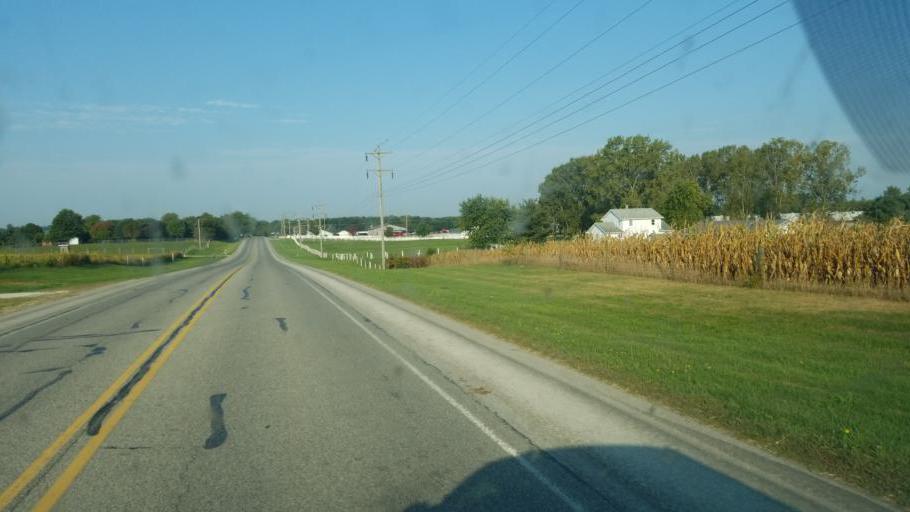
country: US
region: Indiana
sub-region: LaGrange County
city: Topeka
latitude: 41.6550
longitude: -85.5502
